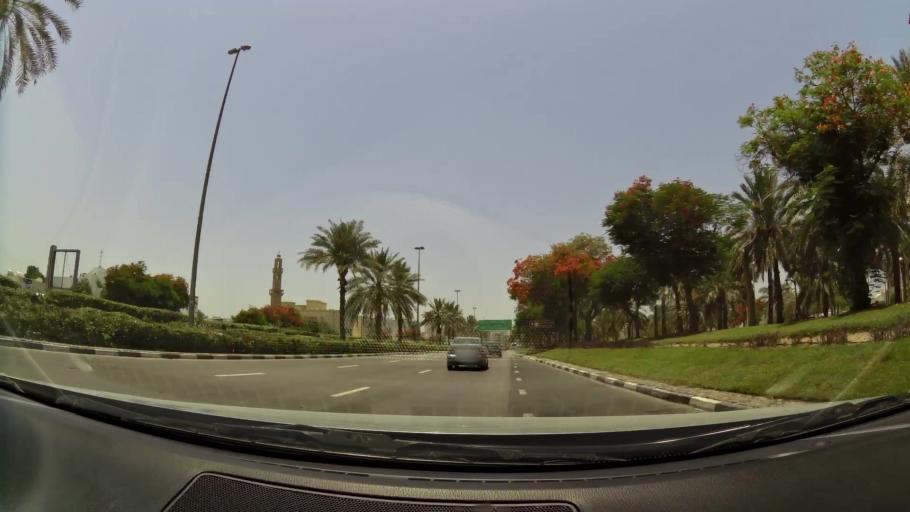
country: AE
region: Ash Shariqah
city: Sharjah
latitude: 25.2333
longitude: 55.2821
